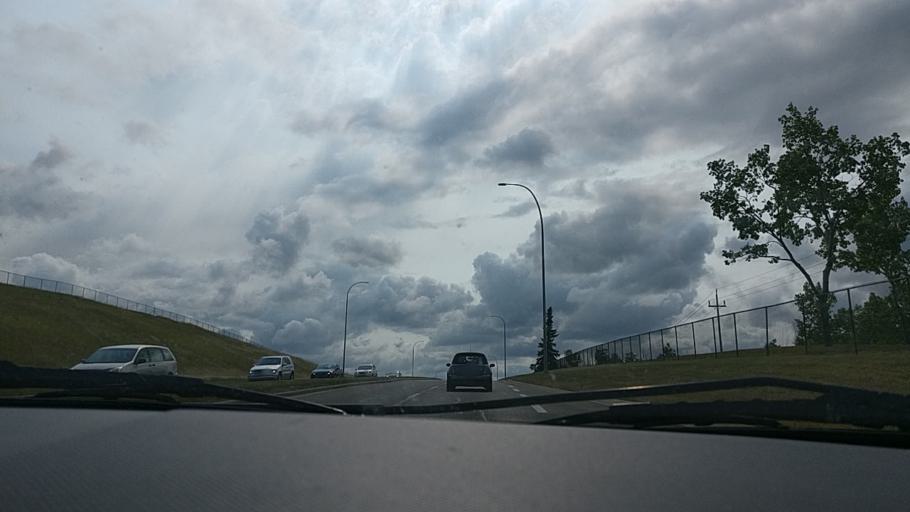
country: CA
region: Alberta
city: Calgary
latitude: 51.1012
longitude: -114.1241
